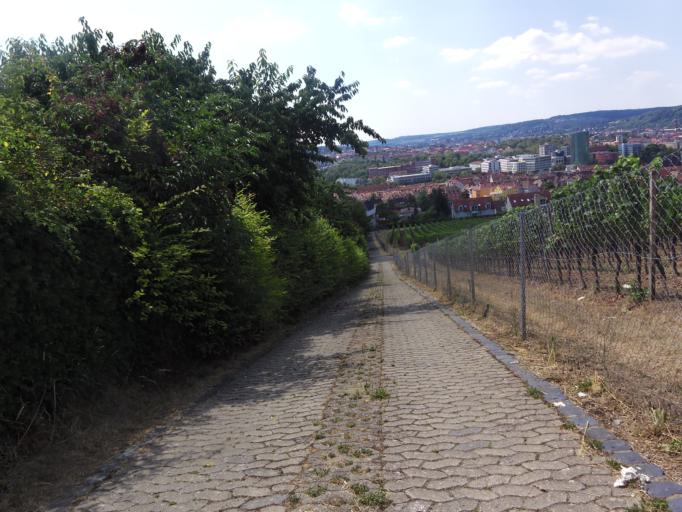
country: DE
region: Bavaria
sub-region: Regierungsbezirk Unterfranken
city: Wuerzburg
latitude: 49.8061
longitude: 9.9511
